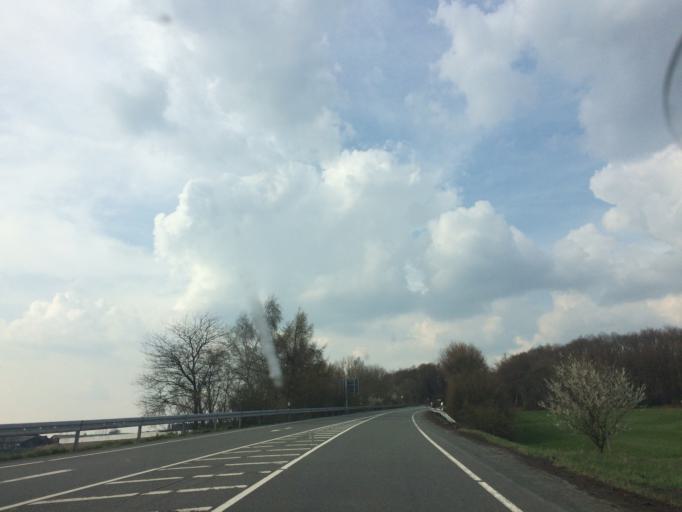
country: DE
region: North Rhine-Westphalia
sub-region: Regierungsbezirk Arnsberg
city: Nachrodt-Wiblingwerde
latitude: 51.2882
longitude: 7.6279
